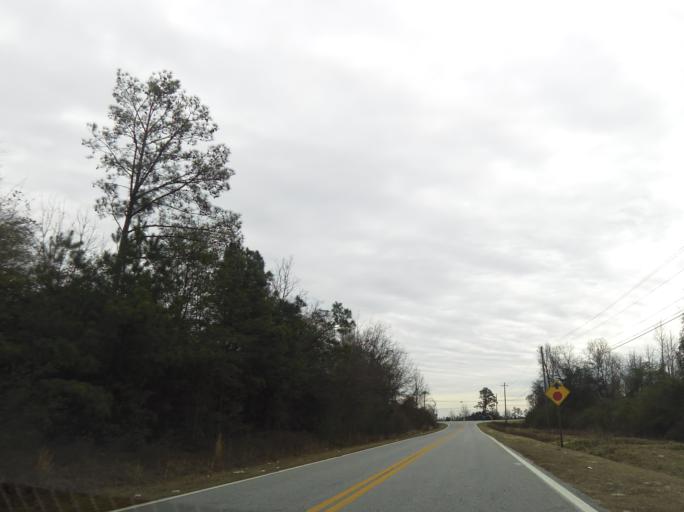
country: US
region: Georgia
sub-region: Bibb County
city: West Point
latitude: 32.8161
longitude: -83.7347
